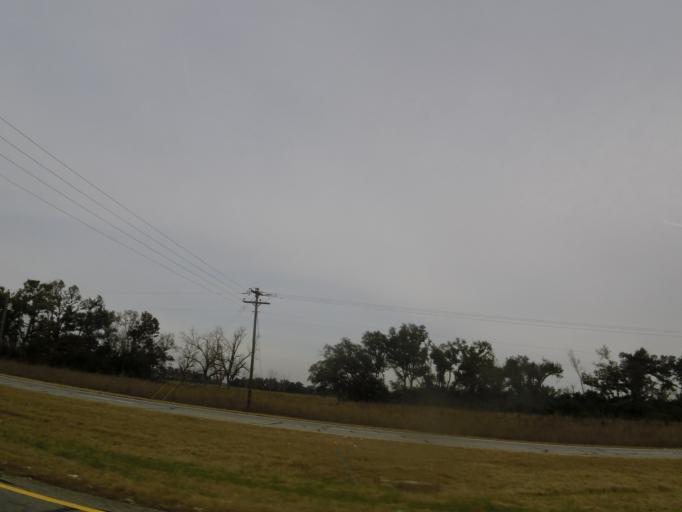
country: US
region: Georgia
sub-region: Seminole County
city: Donalsonville
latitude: 30.9695
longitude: -84.7314
